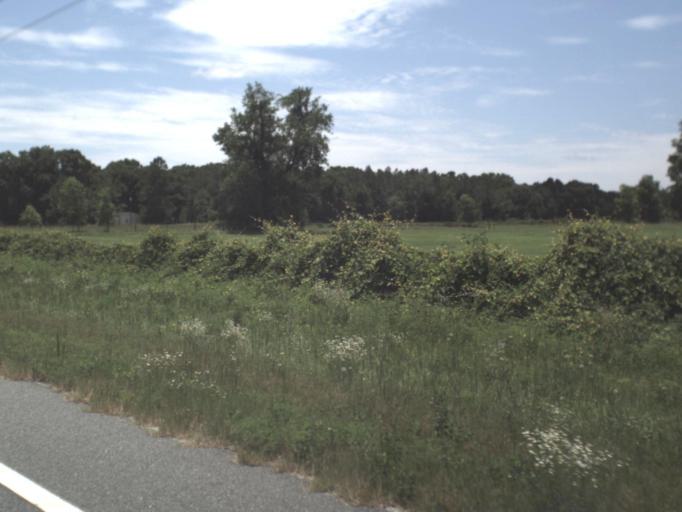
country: US
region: Florida
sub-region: Dixie County
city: Cross City
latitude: 29.7330
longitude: -82.9846
